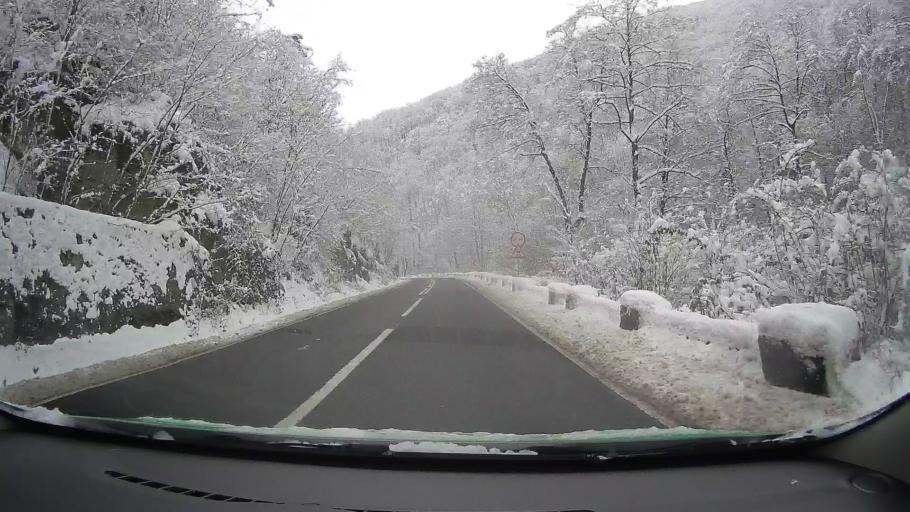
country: RO
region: Alba
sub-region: Comuna Sasciori
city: Sasciori
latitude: 45.8550
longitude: 23.5862
